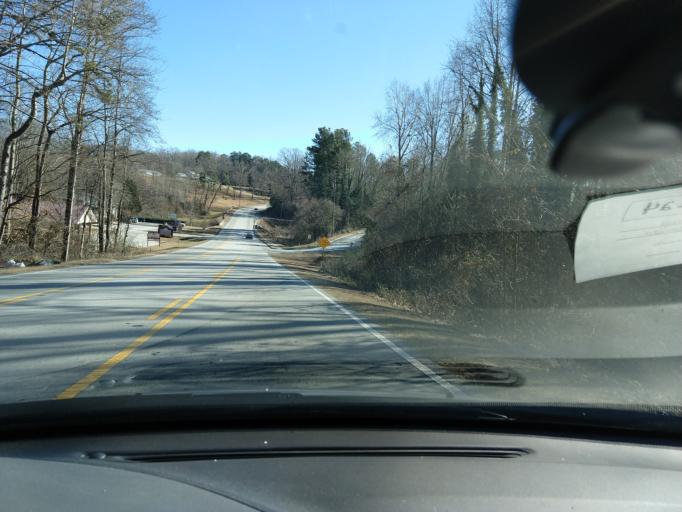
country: US
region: Georgia
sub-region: Stephens County
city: Toccoa
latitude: 34.5947
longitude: -83.3468
